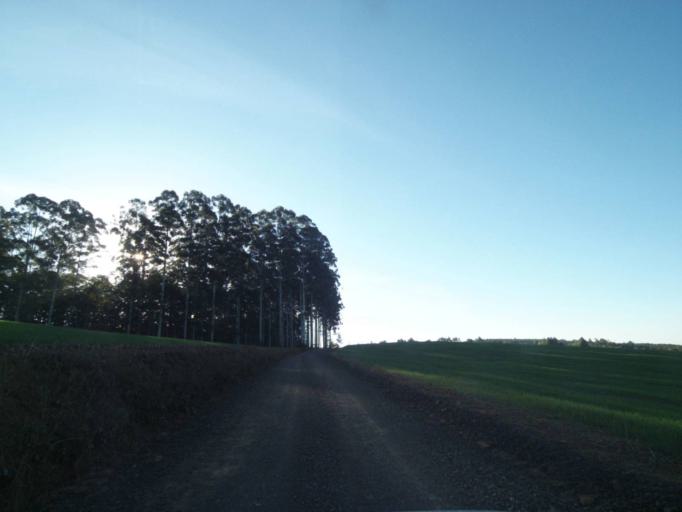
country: BR
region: Parana
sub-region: Telemaco Borba
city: Telemaco Borba
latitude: -24.4604
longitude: -50.5992
